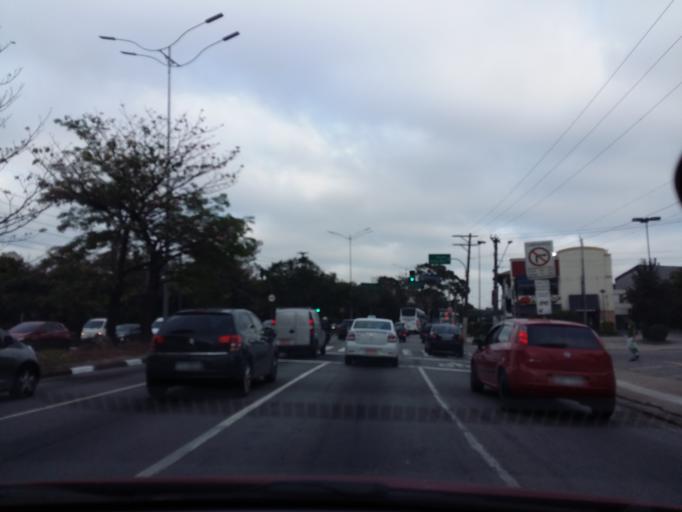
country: BR
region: Sao Paulo
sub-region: Sao Paulo
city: Sao Paulo
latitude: -23.6155
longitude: -46.6669
